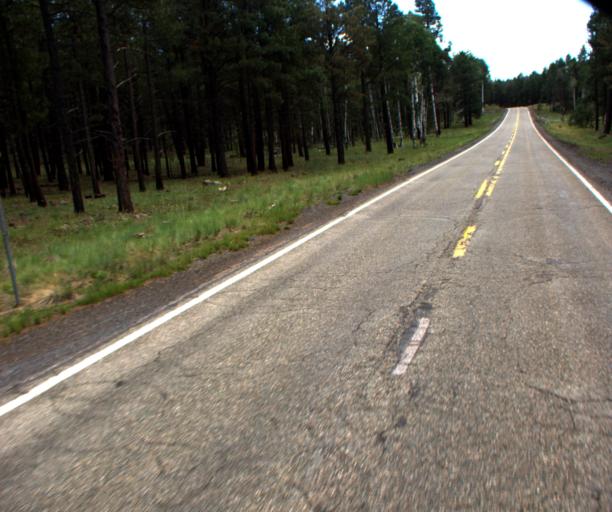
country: US
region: Arizona
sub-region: Coconino County
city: Parks
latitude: 35.3433
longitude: -111.7883
